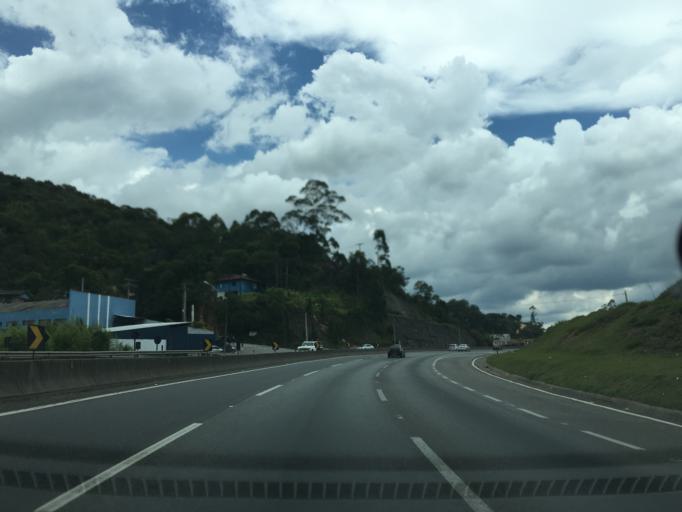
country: BR
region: Sao Paulo
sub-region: Mairipora
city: Mairipora
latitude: -23.2857
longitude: -46.5901
